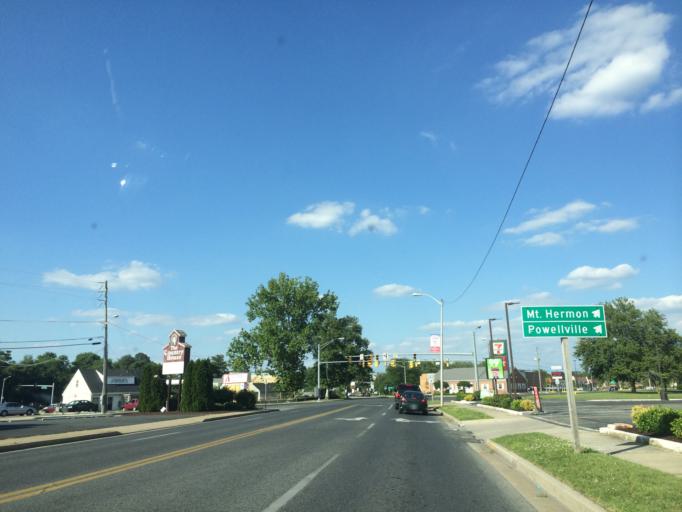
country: US
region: Maryland
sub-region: Wicomico County
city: Salisbury
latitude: 38.3673
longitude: -75.5838
